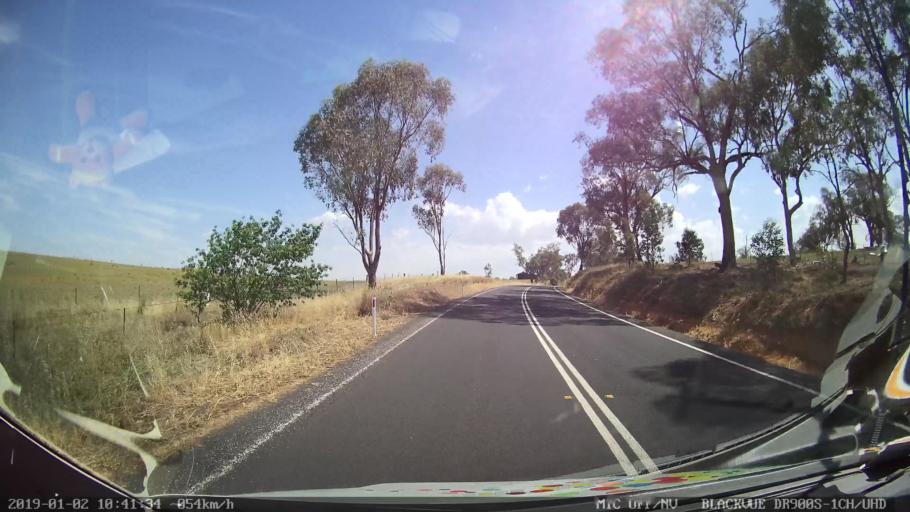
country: AU
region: New South Wales
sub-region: Cootamundra
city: Cootamundra
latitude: -34.7930
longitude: 148.3066
